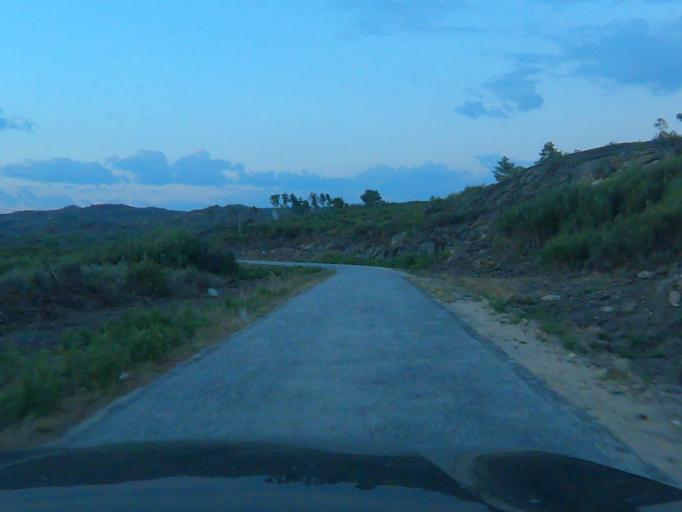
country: PT
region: Vila Real
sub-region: Sabrosa
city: Sabrosa
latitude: 41.2790
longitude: -7.6252
